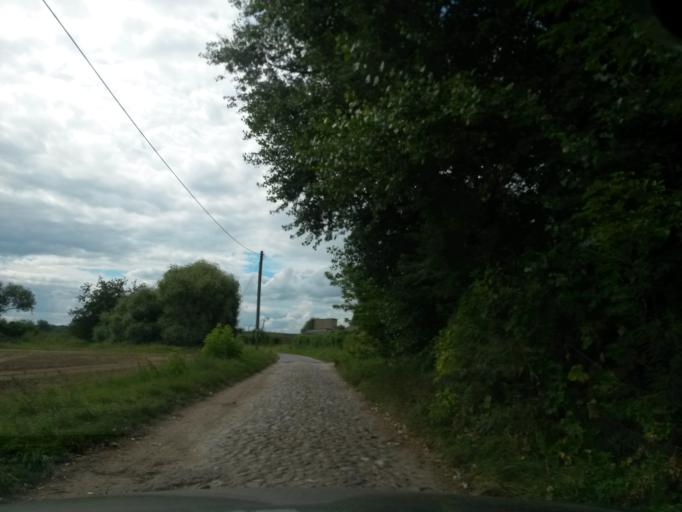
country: DE
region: Brandenburg
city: Oderberg
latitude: 52.8638
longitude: 14.0763
